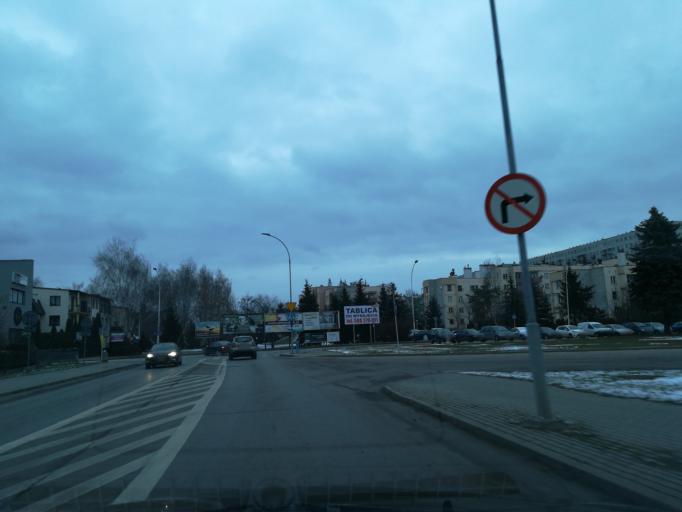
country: PL
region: Subcarpathian Voivodeship
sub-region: Rzeszow
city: Rzeszow
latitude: 50.0210
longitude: 22.0128
